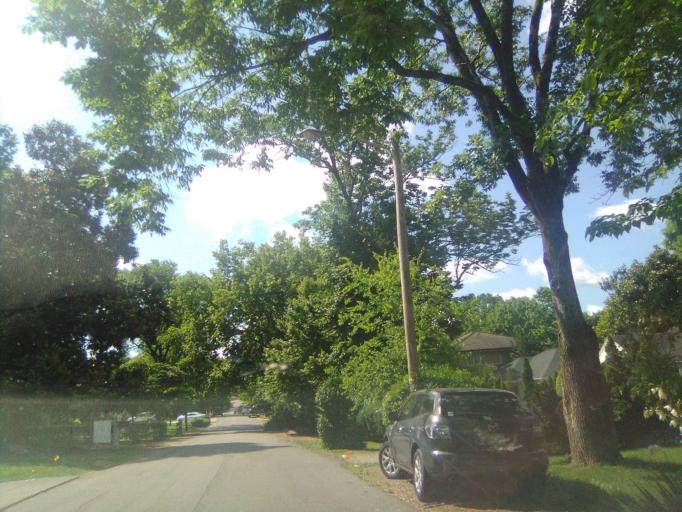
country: US
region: Tennessee
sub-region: Davidson County
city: Belle Meade
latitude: 36.1005
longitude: -86.8648
